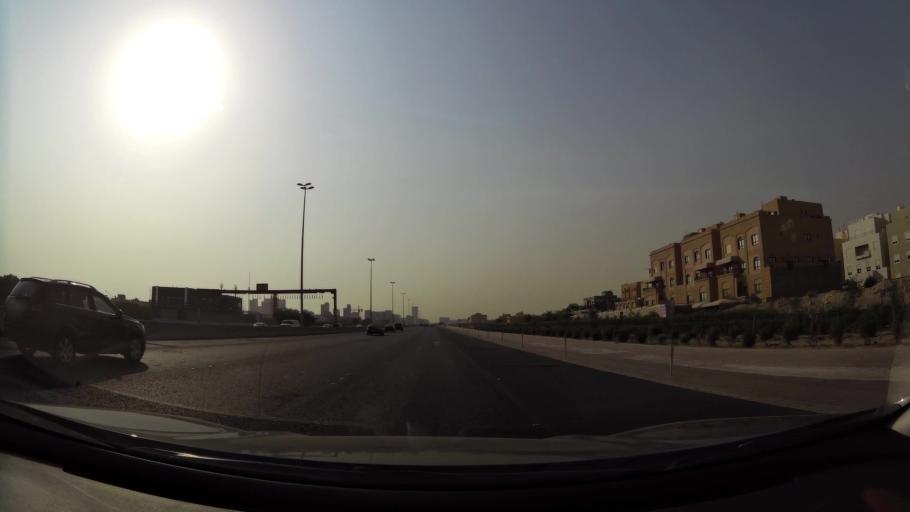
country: KW
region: Al Ahmadi
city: Al Fintas
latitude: 29.1925
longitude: 48.1093
